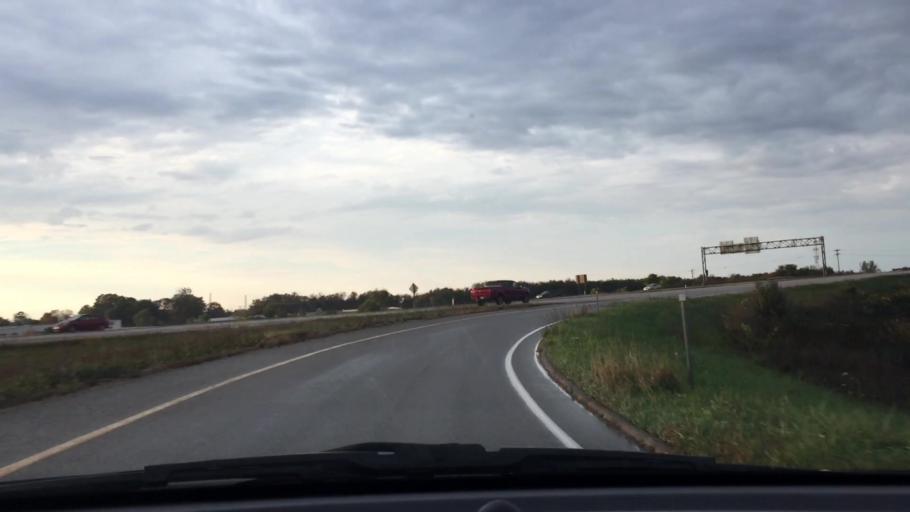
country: US
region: Wisconsin
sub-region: Walworth County
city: Elkhorn
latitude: 42.6730
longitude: -88.5241
